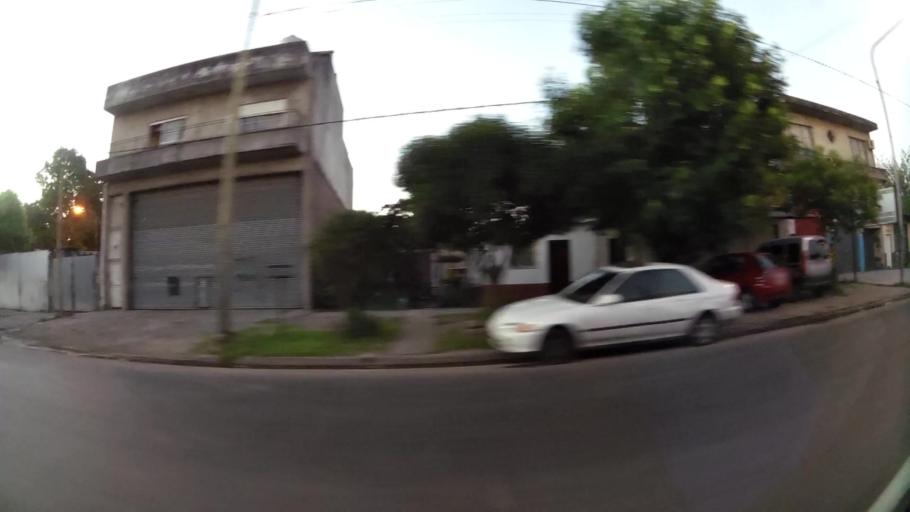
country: AR
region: Buenos Aires
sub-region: Partido de Moron
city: Moron
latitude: -34.7037
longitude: -58.6146
